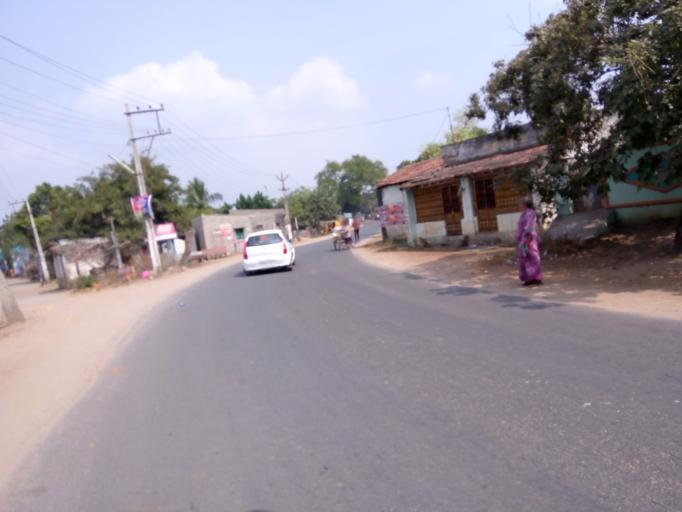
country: IN
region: Andhra Pradesh
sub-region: Prakasam
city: Chirala
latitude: 15.8519
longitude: 80.3896
